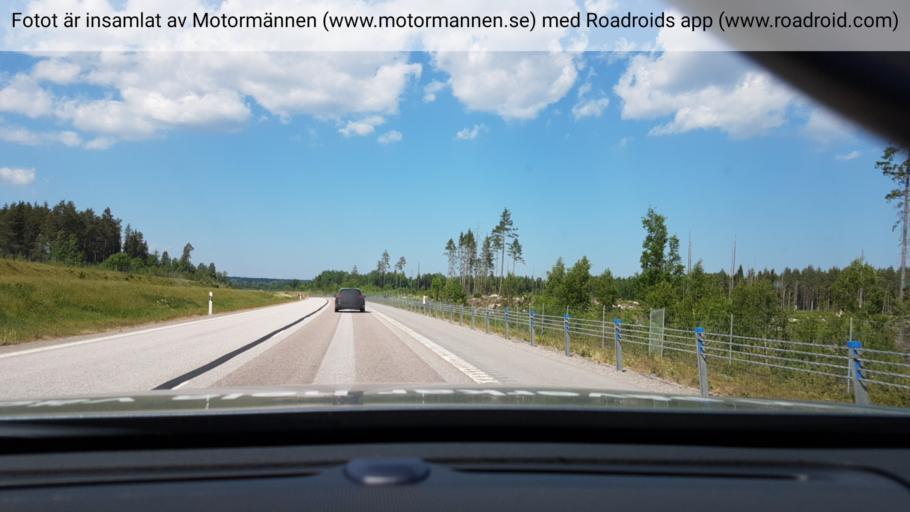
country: SE
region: Uppsala
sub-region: Tierps Kommun
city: Tierp
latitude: 60.3116
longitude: 17.5217
